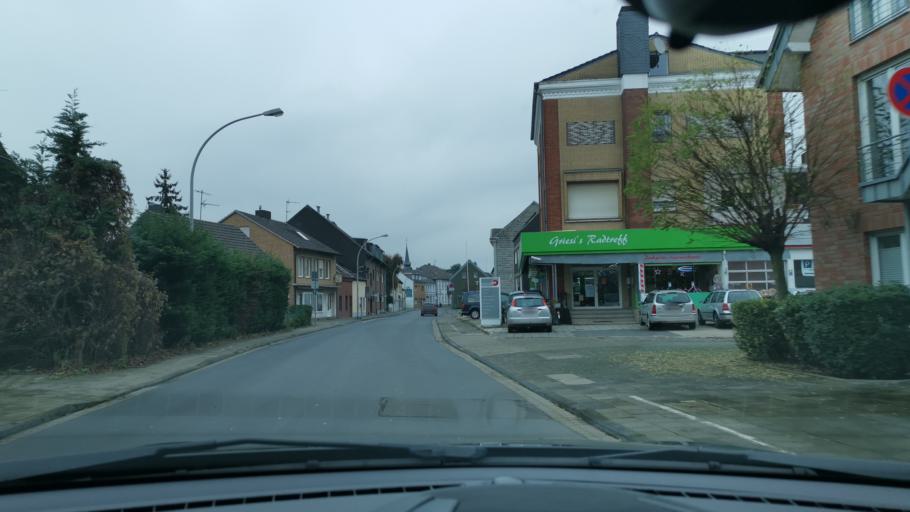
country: DE
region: North Rhine-Westphalia
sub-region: Regierungsbezirk Dusseldorf
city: Grevenbroich
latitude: 51.1015
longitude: 6.6155
